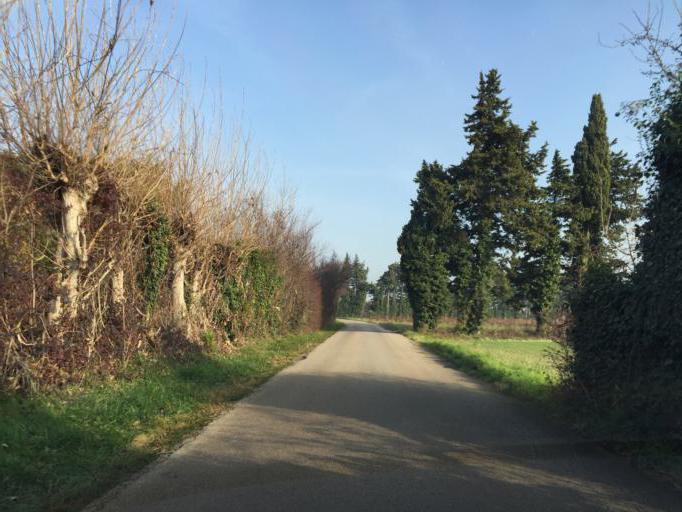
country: FR
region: Provence-Alpes-Cote d'Azur
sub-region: Departement du Vaucluse
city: Courthezon
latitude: 44.0849
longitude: 4.9083
